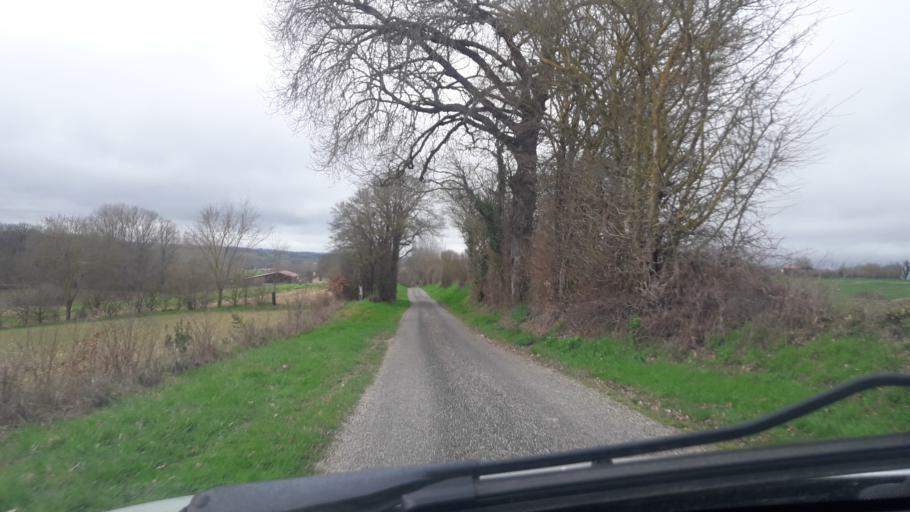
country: FR
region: Midi-Pyrenees
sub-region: Departement du Gers
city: Gimont
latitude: 43.6568
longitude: 0.9609
